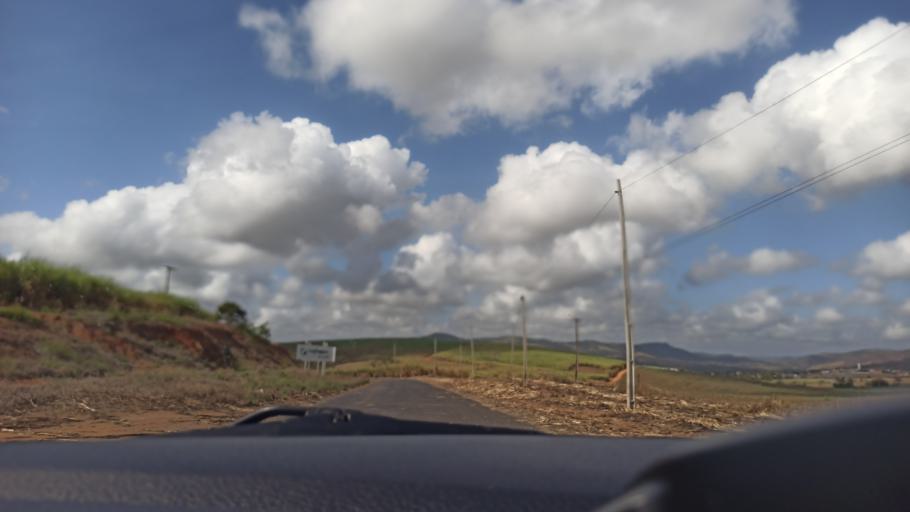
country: BR
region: Paraiba
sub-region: Juripiranga
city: Juripiranga
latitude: -7.3930
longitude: -35.2563
